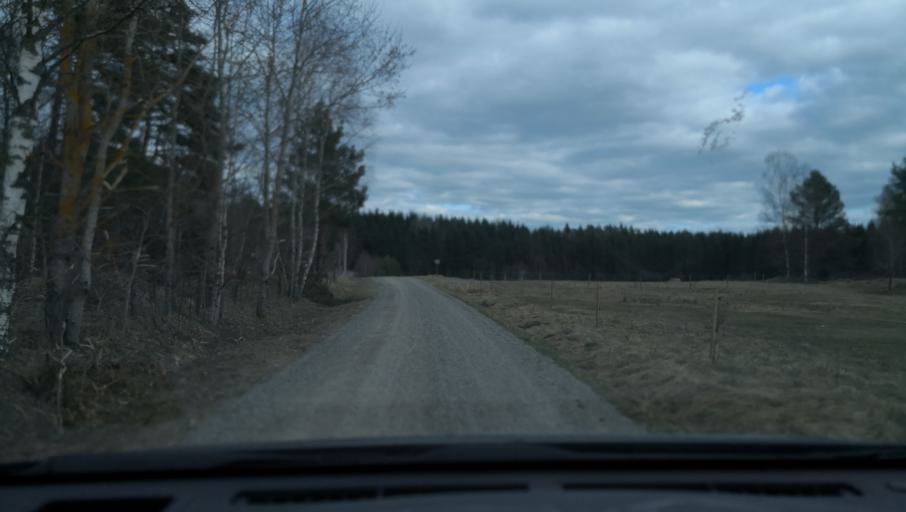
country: SE
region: Soedermanland
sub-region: Katrineholms Kommun
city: Katrineholm
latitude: 59.1314
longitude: 16.1759
